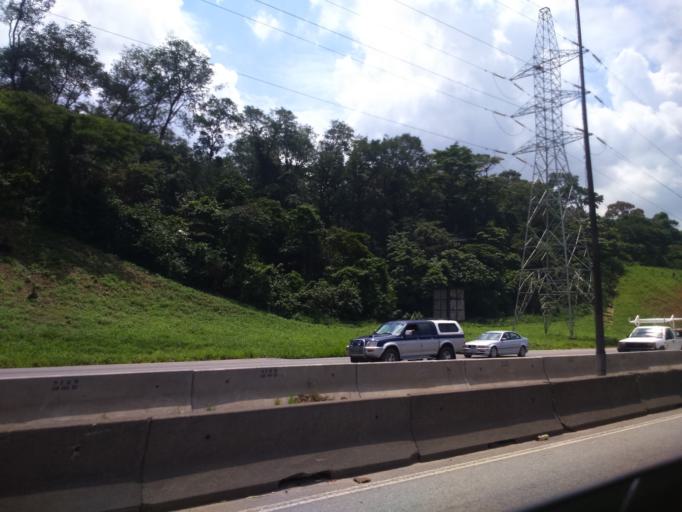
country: CI
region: Lagunes
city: Abidjan
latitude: 5.3579
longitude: -4.0520
